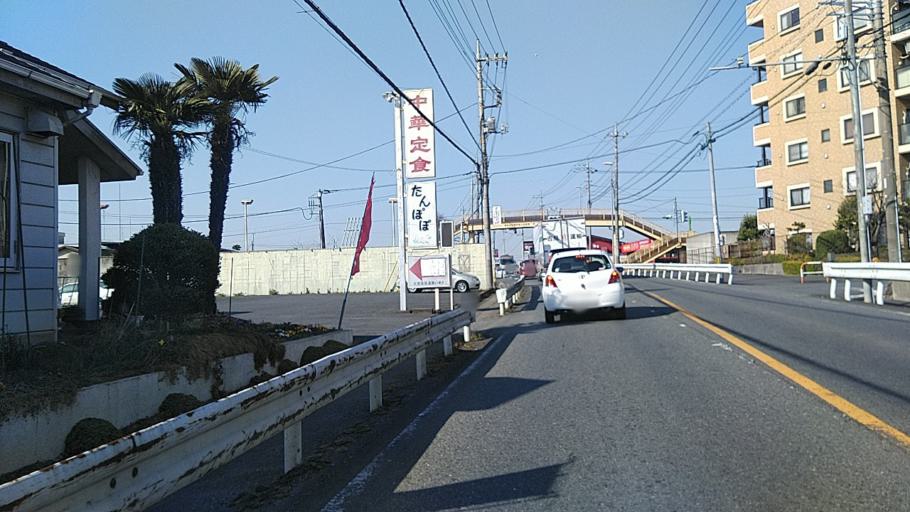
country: JP
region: Saitama
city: Fukiage-fujimi
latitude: 36.0646
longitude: 139.4083
